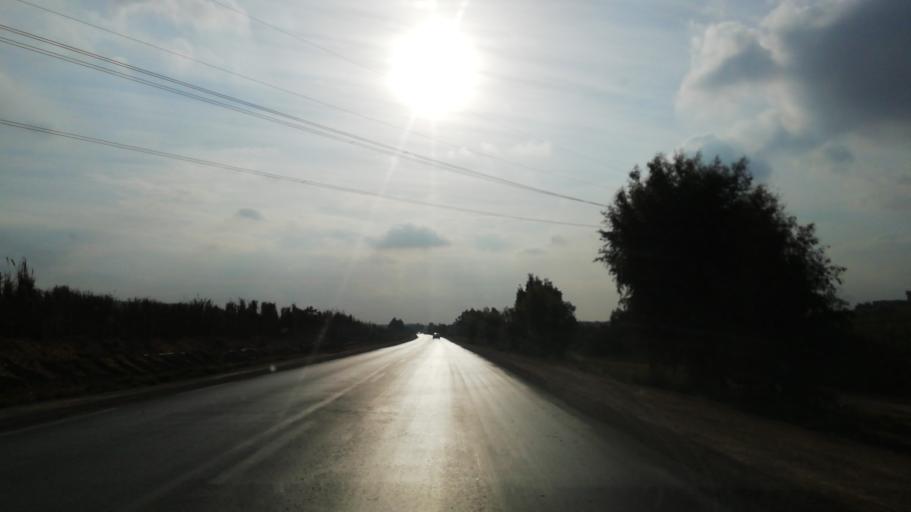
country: DZ
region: Mostaganem
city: Mostaganem
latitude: 35.8452
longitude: 0.0689
